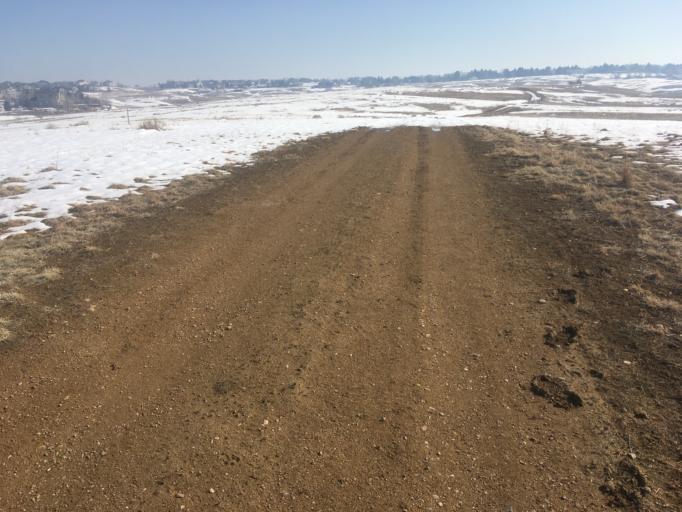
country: US
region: Colorado
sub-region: Boulder County
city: Lafayette
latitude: 39.9716
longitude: -105.0583
